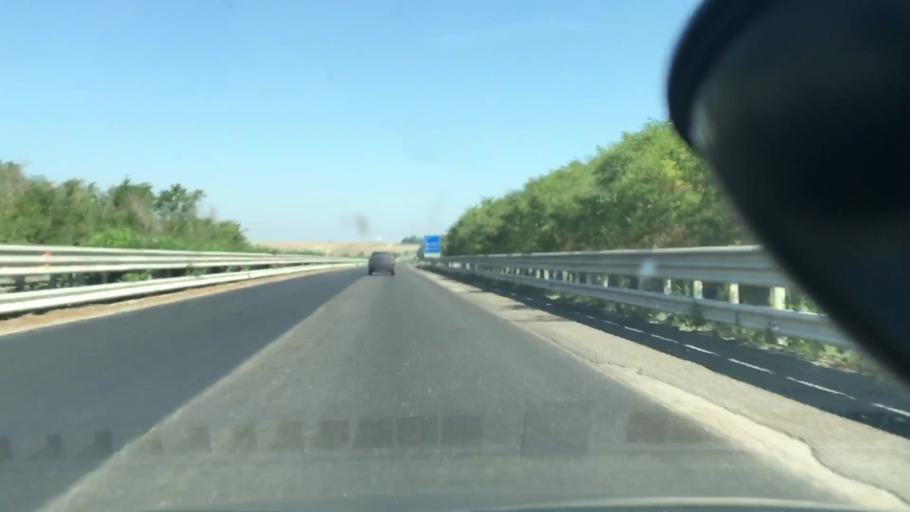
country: IT
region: Apulia
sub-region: Provincia di Foggia
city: Ordona
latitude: 41.2956
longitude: 15.5542
